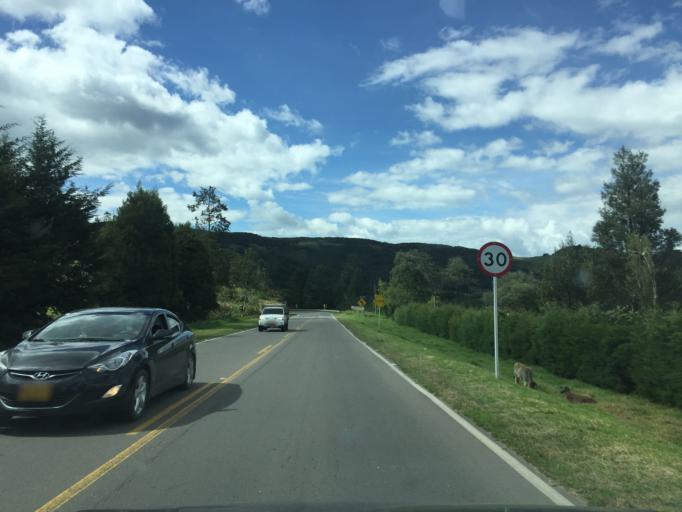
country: CO
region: Boyaca
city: Arcabuco
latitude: 5.7890
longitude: -73.4642
